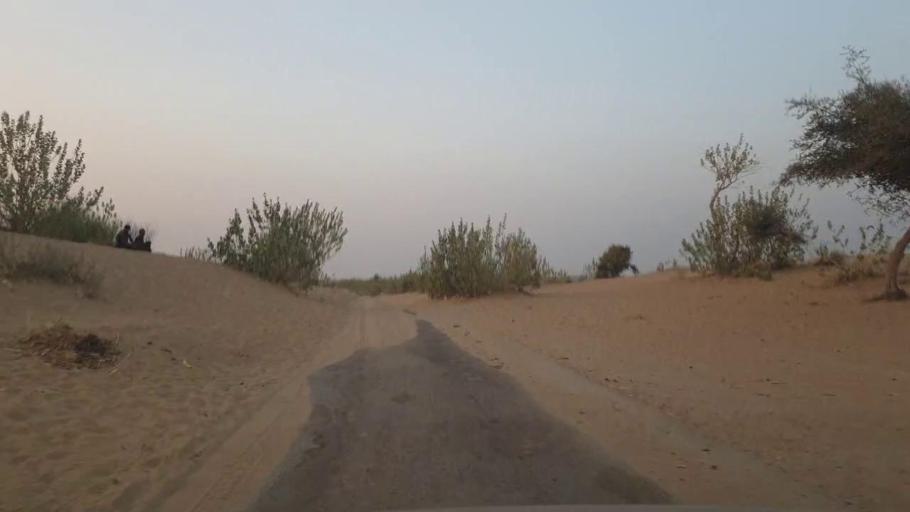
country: PK
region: Sindh
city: Umarkot
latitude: 25.2926
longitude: 70.0770
